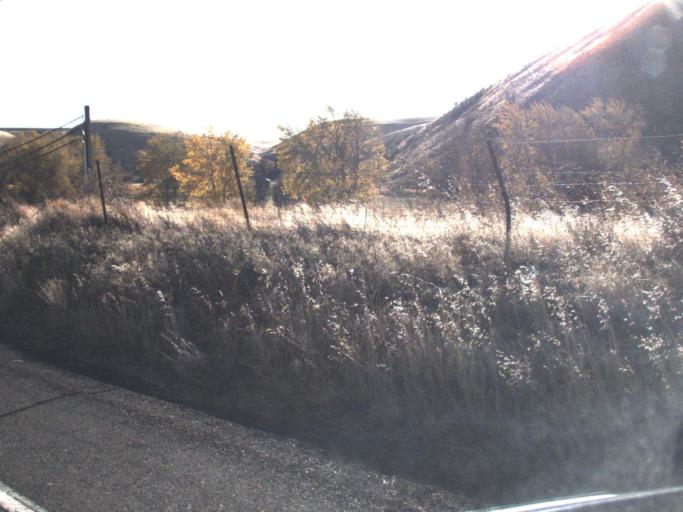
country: US
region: Washington
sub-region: Garfield County
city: Pomeroy
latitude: 46.4720
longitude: -117.5263
